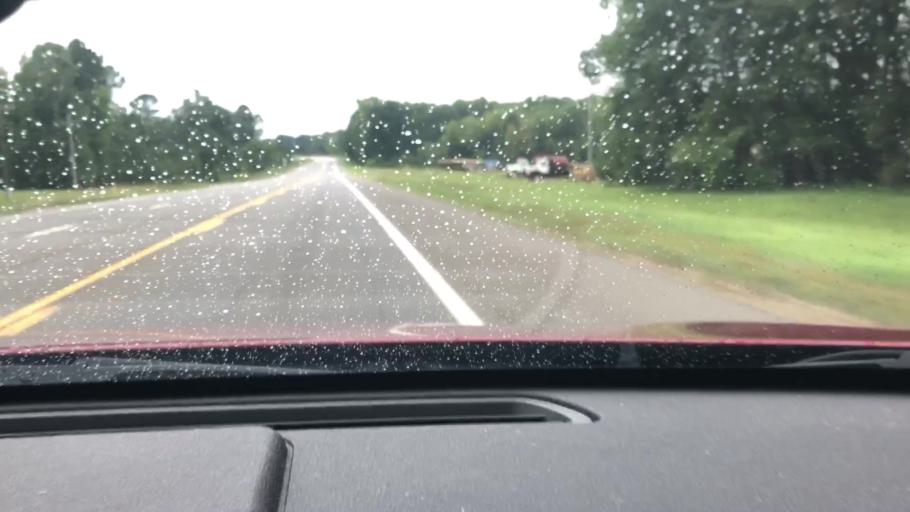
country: US
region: Arkansas
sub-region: Lafayette County
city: Stamps
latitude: 33.3636
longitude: -93.4685
